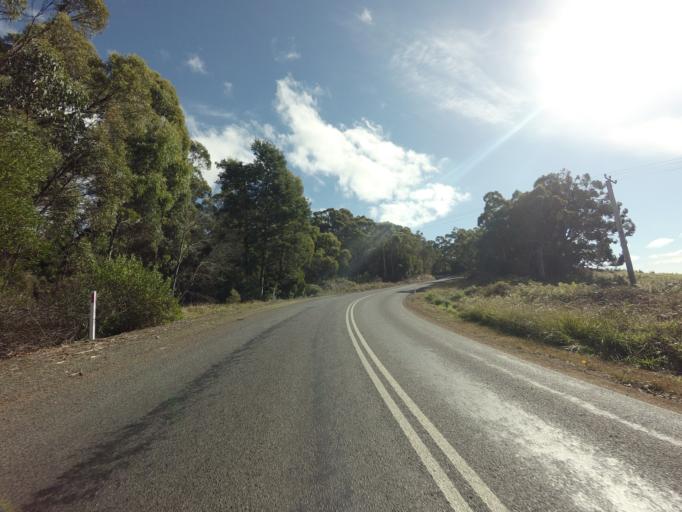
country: AU
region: Tasmania
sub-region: Clarence
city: Sandford
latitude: -43.0557
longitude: 147.8031
